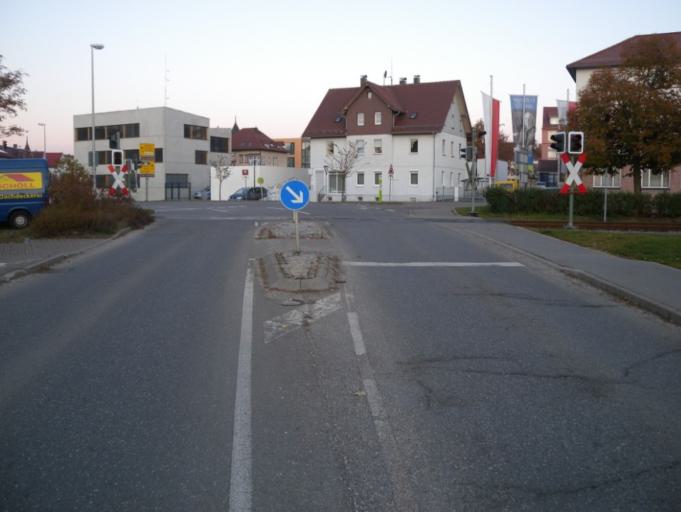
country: DE
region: Baden-Wuerttemberg
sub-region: Tuebingen Region
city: Munsingen
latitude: 48.4109
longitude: 9.4909
